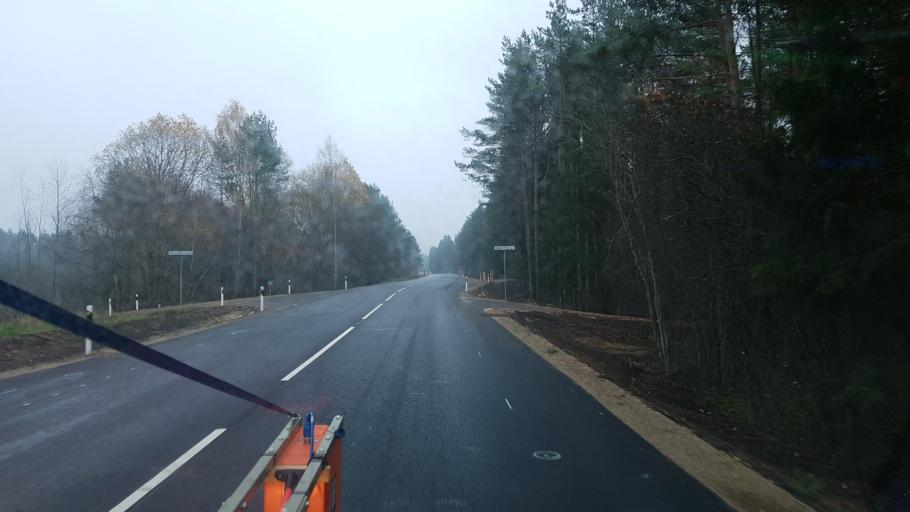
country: EE
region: Raplamaa
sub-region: Kohila vald
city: Kohila
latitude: 59.1803
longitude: 24.7835
